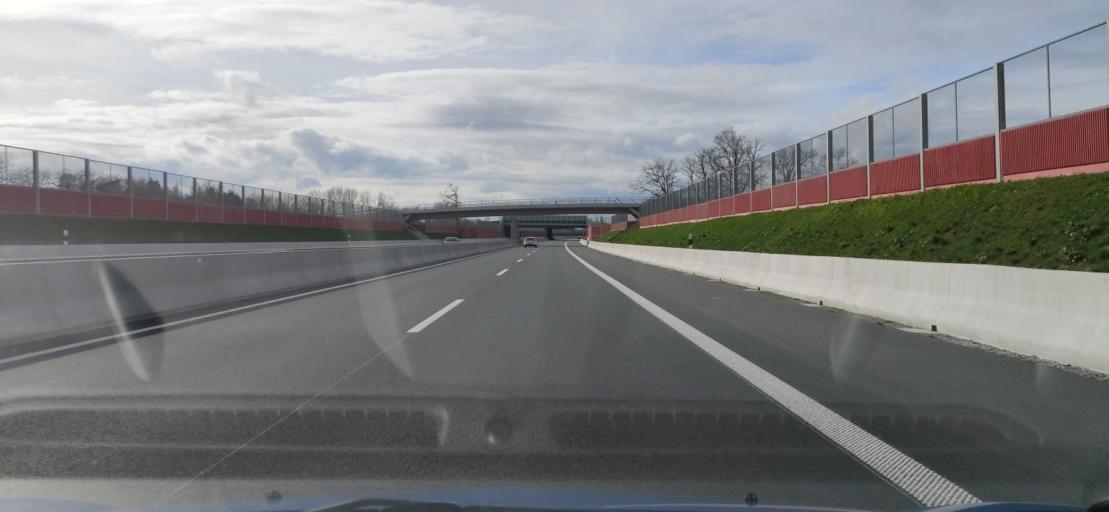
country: DE
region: North Rhine-Westphalia
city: Borgholzhausen
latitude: 52.0684
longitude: 8.2803
